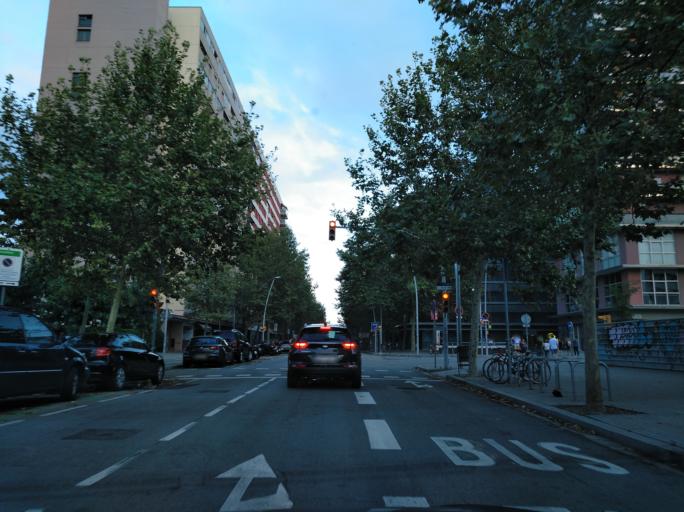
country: ES
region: Catalonia
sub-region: Provincia de Barcelona
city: Sant Marti
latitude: 41.4087
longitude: 2.2092
